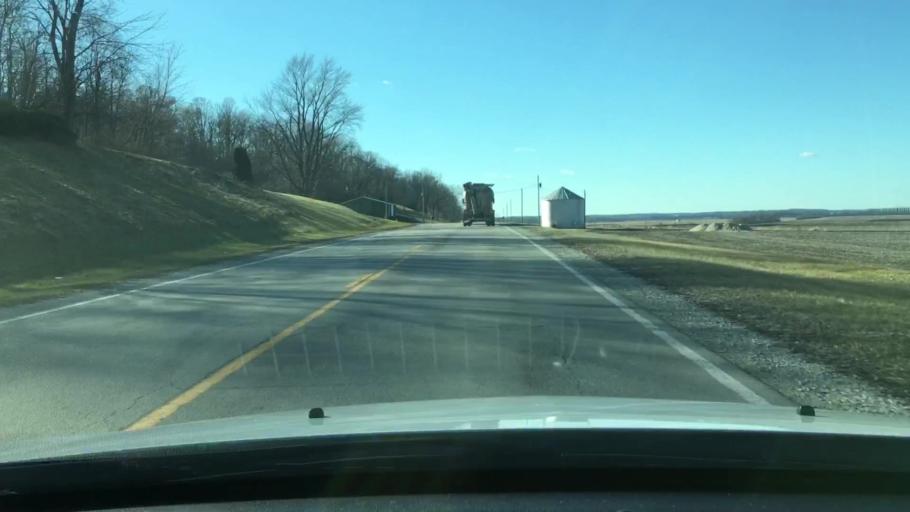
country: US
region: Illinois
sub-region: Morgan County
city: Meredosia
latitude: 39.7449
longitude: -90.5403
